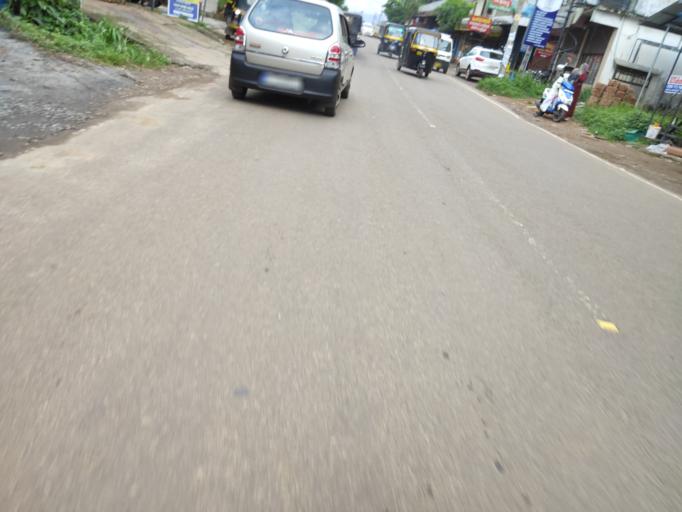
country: IN
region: Kerala
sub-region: Malappuram
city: Manjeri
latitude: 11.1949
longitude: 76.2384
